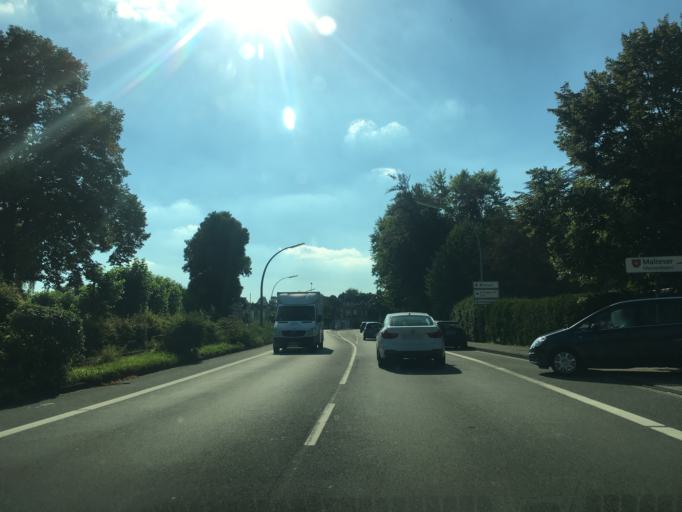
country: DE
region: North Rhine-Westphalia
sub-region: Regierungsbezirk Munster
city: Warendorf
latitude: 51.9498
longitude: 7.9972
